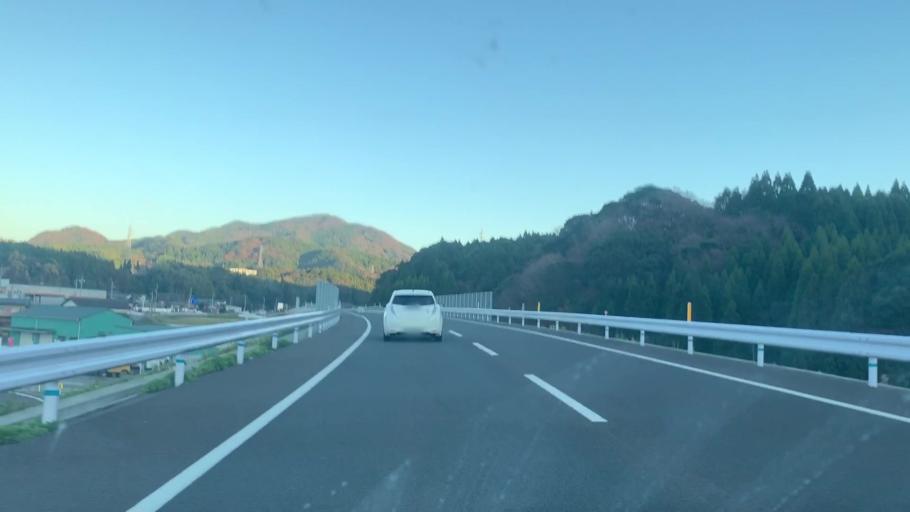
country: JP
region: Saga Prefecture
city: Takeocho-takeo
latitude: 33.2502
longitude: 129.9937
